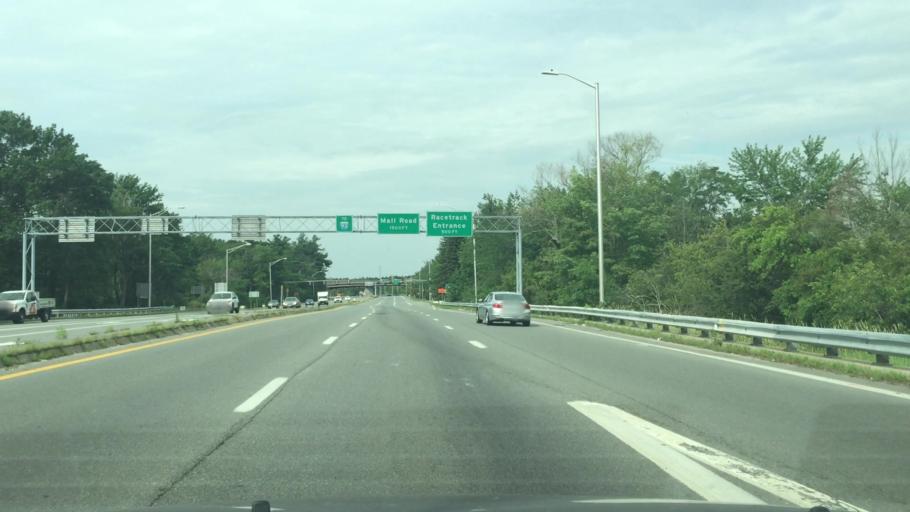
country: US
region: New Hampshire
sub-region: Rockingham County
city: Salem
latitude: 42.7690
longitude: -71.2211
